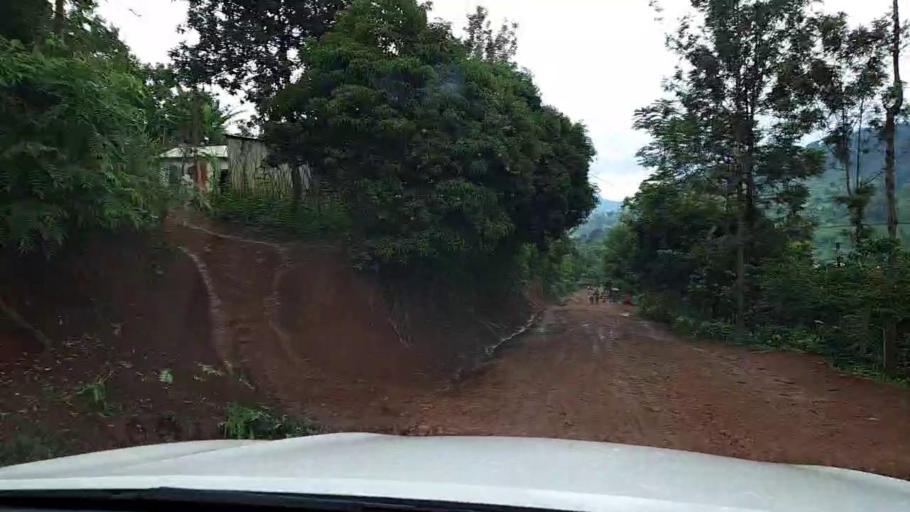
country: RW
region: Western Province
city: Cyangugu
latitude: -2.5679
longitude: 29.0329
